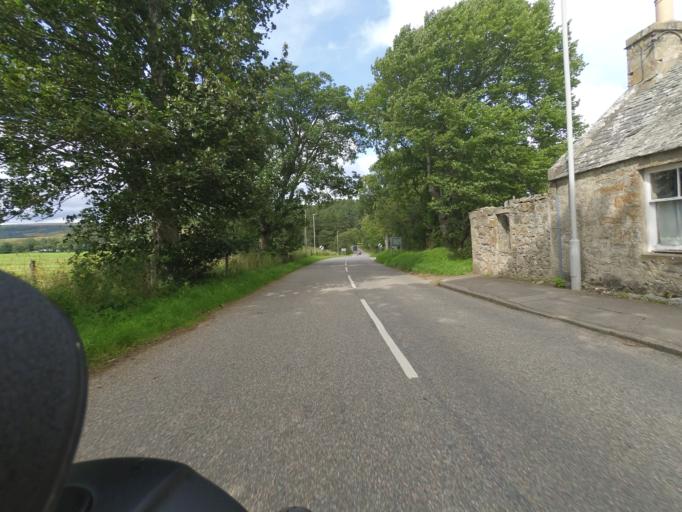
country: GB
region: Scotland
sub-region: Highland
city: Grantown on Spey
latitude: 57.2563
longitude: -3.3855
